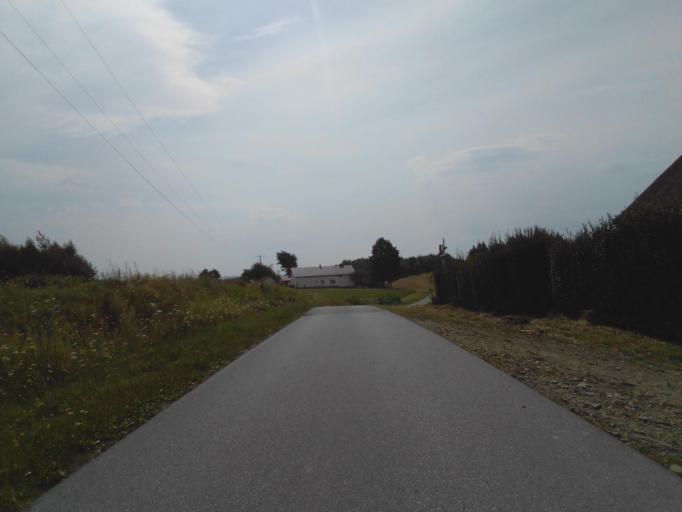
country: PL
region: Subcarpathian Voivodeship
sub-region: Powiat strzyzowski
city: Frysztak
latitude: 49.8655
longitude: 21.5315
